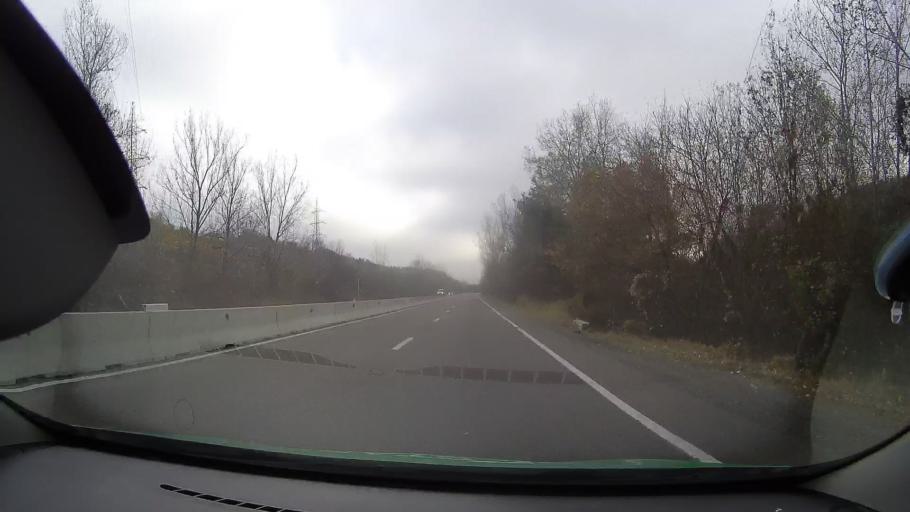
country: RO
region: Prahova
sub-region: Municipiul Campina
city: Campina
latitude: 45.1170
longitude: 25.7308
